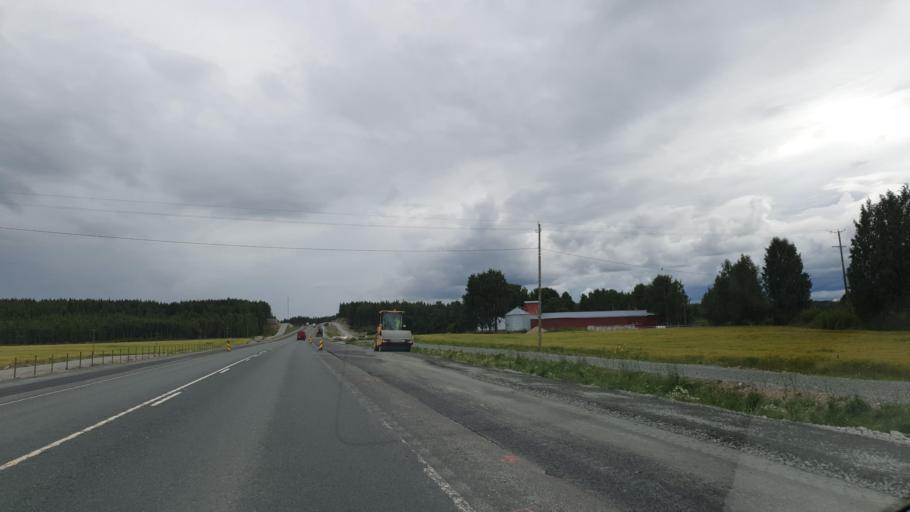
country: FI
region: Northern Savo
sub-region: Ylae-Savo
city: Lapinlahti
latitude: 63.2899
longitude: 27.4543
